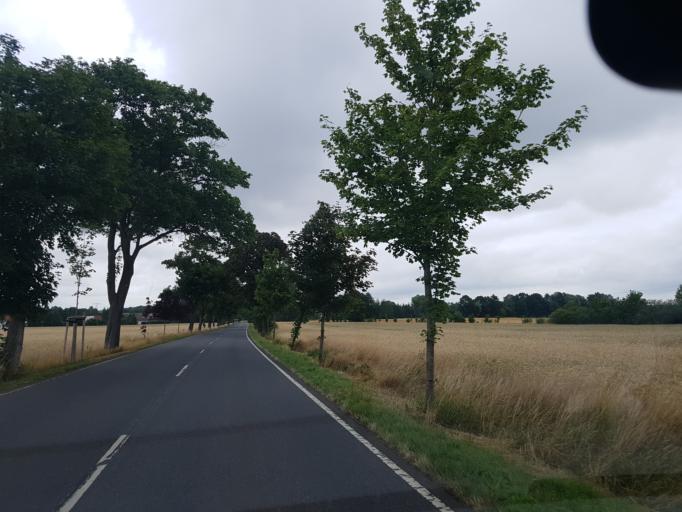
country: DE
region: Brandenburg
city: Luckau
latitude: 51.8357
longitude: 13.6880
